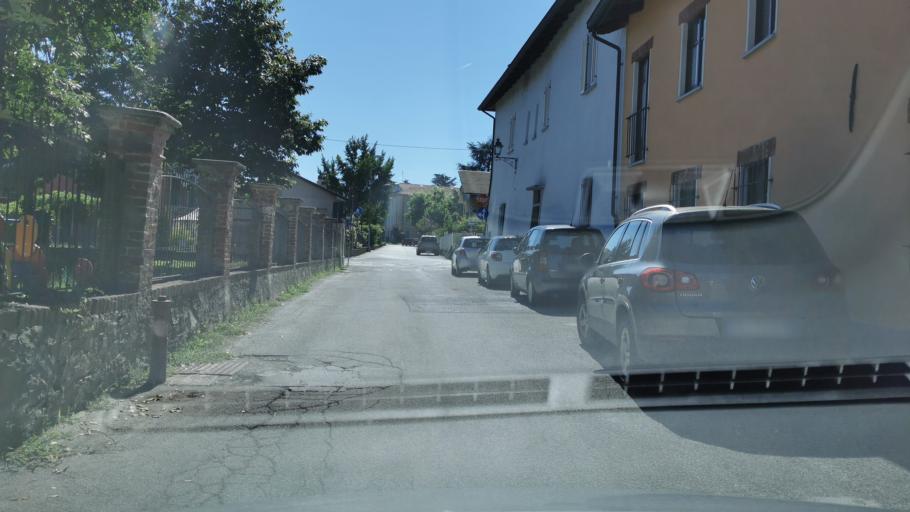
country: IT
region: Piedmont
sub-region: Provincia di Cuneo
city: Boves
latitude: 44.3280
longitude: 7.5533
